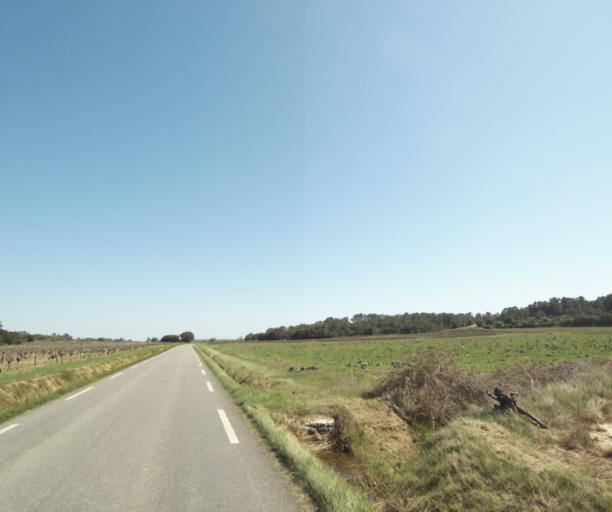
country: FR
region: Languedoc-Roussillon
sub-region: Departement de l'Herault
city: Saint-Drezery
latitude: 43.7467
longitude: 3.9664
